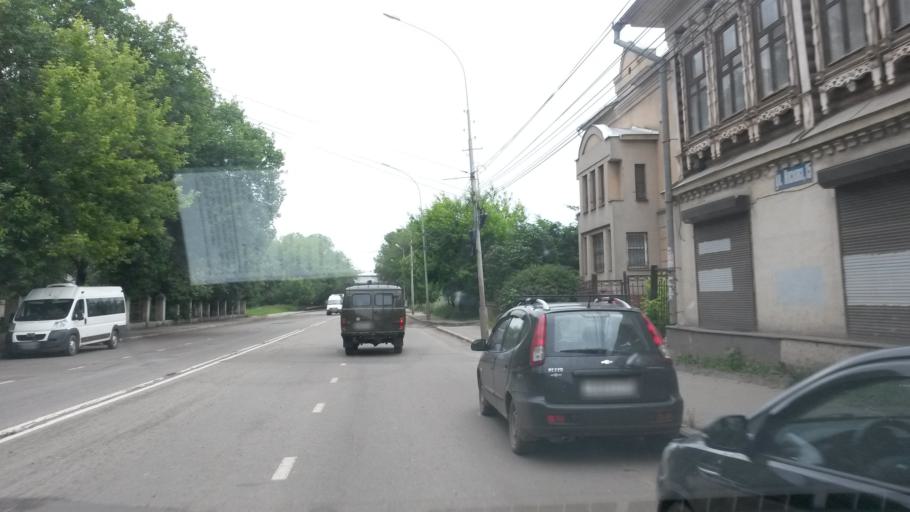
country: RU
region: Jaroslavl
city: Yaroslavl
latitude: 57.6081
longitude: 39.8391
